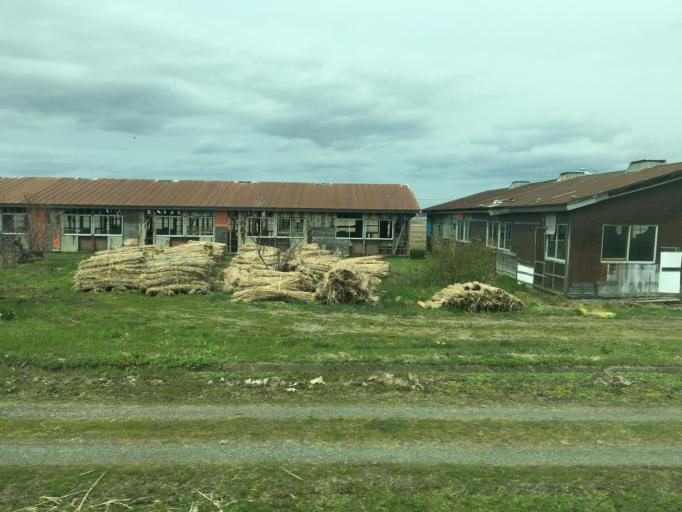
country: JP
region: Aomori
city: Shimokizukuri
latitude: 40.7901
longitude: 140.3689
